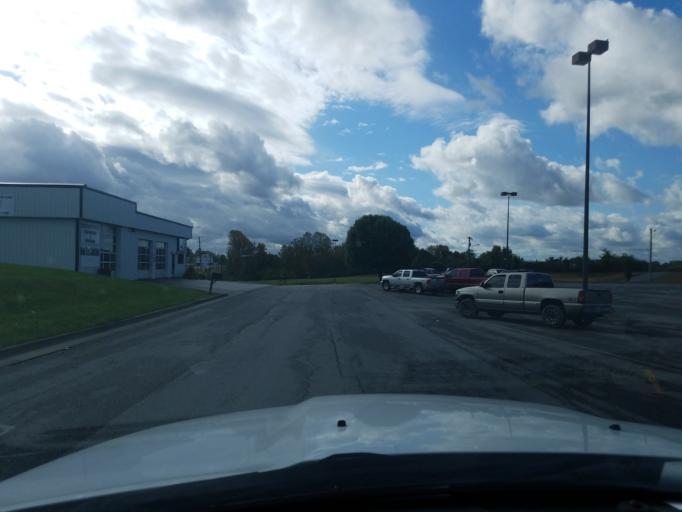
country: US
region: Kentucky
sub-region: Russell County
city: Russell Springs
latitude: 37.0615
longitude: -85.0717
